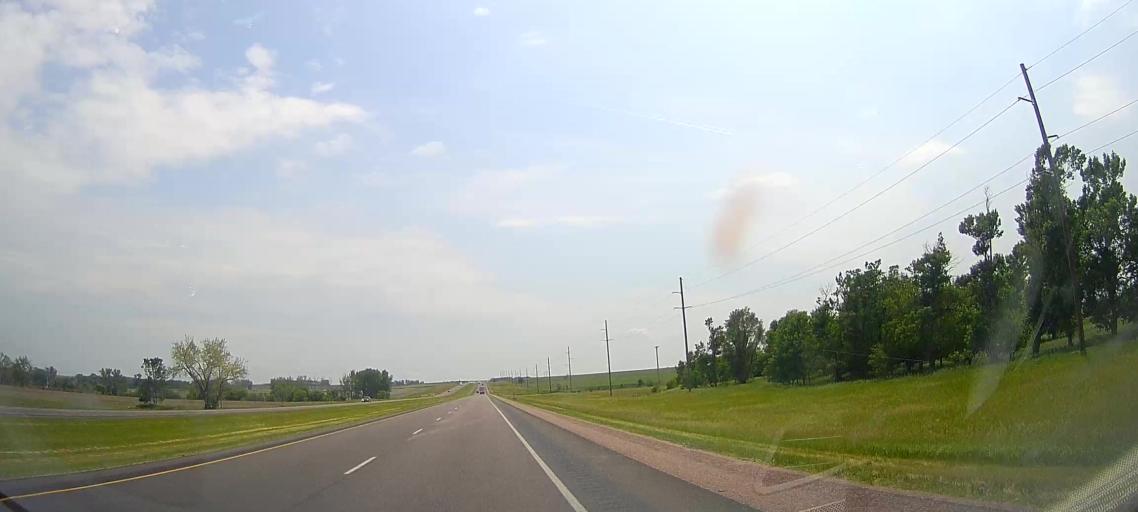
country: US
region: South Dakota
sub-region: Union County
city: Beresford
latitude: 43.1861
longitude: -96.7965
